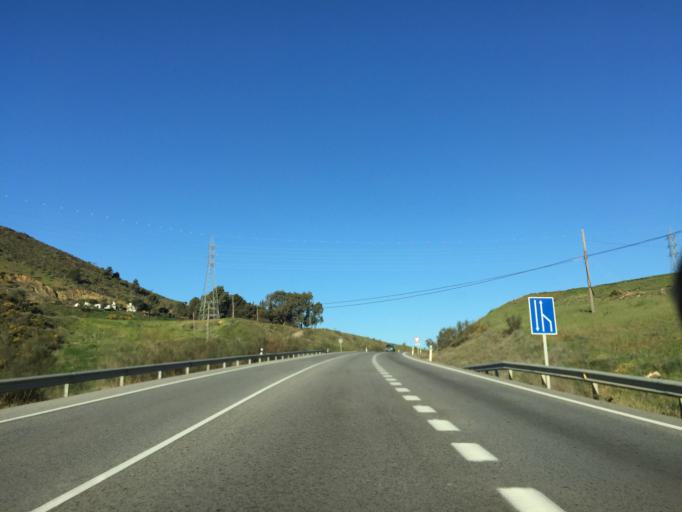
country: ES
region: Andalusia
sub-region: Provincia de Malaga
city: Ardales
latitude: 36.8615
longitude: -4.8372
